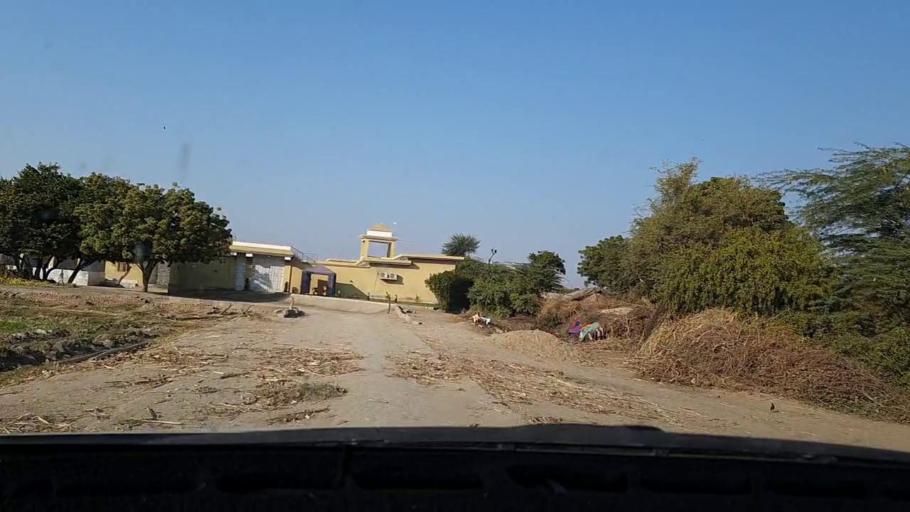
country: PK
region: Sindh
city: Tando Mittha Khan
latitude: 25.8575
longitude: 69.3334
